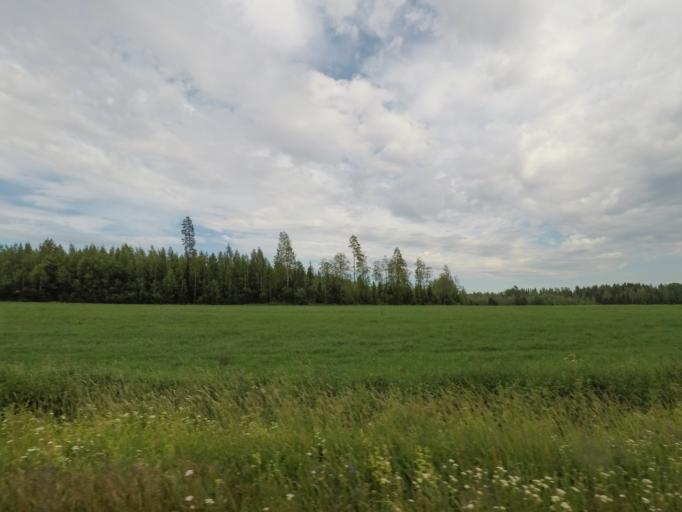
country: FI
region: Paijanne Tavastia
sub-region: Lahti
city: Hollola
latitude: 60.8260
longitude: 25.4884
